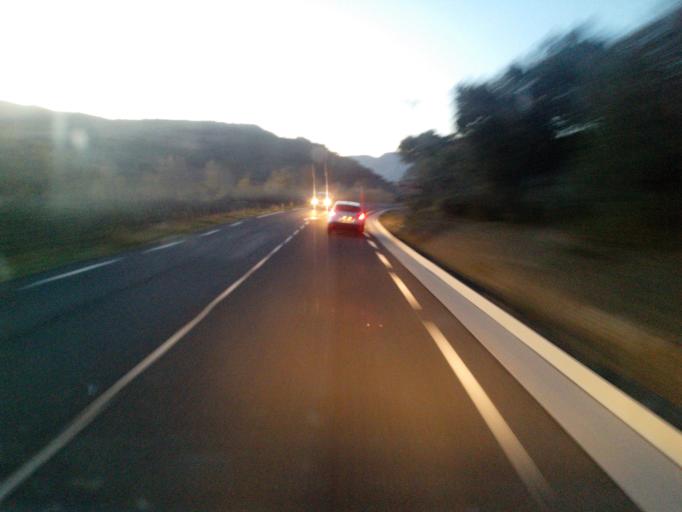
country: FR
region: Languedoc-Roussillon
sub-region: Departement des Pyrenees-Orientales
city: Estagel
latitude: 42.7822
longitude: 2.6886
